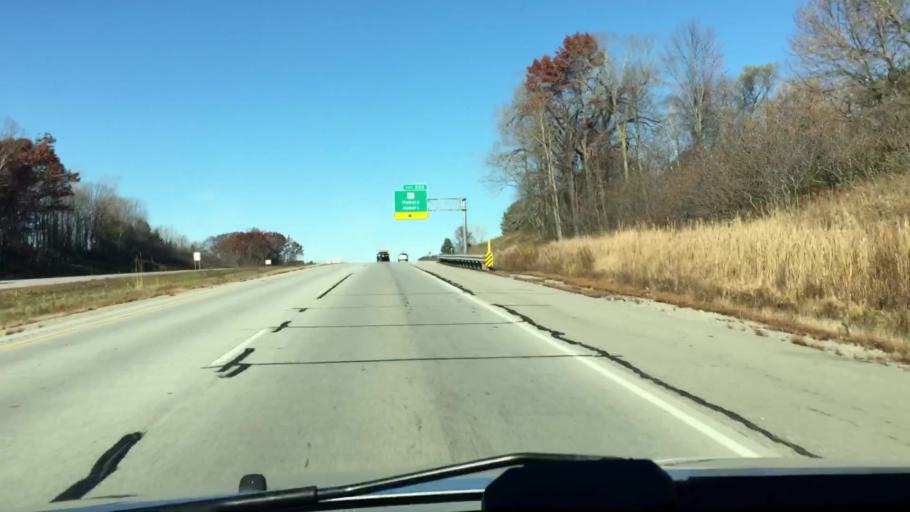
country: US
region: Wisconsin
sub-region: Brown County
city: Howard
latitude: 44.5552
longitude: -88.1173
